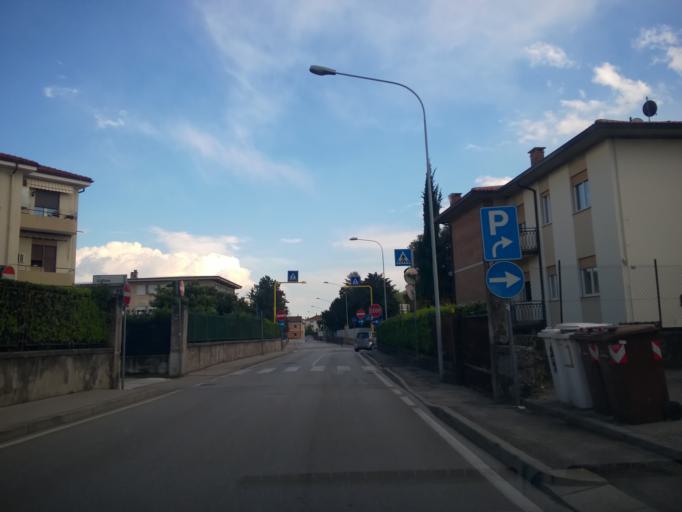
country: IT
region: Veneto
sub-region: Provincia di Vicenza
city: Thiene
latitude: 45.7064
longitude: 11.4856
